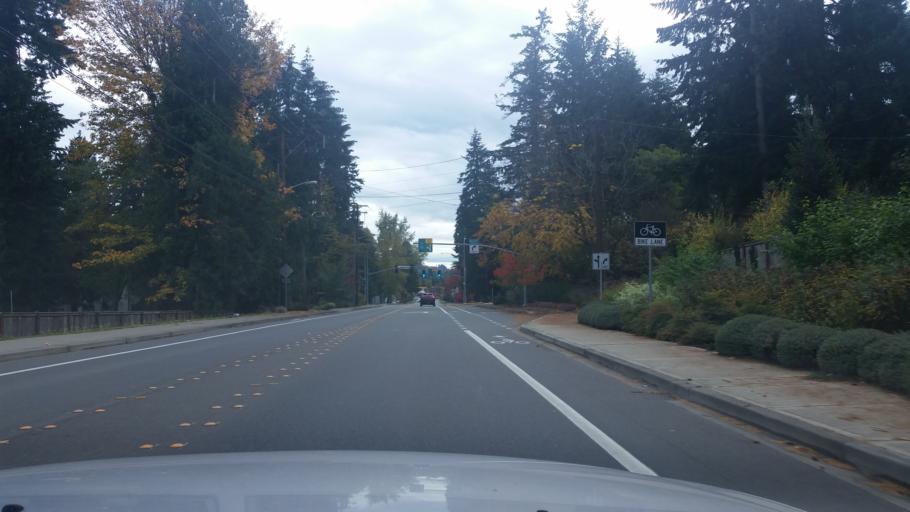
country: US
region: Washington
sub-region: King County
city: Eastgate
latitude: 47.5903
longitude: -122.1463
